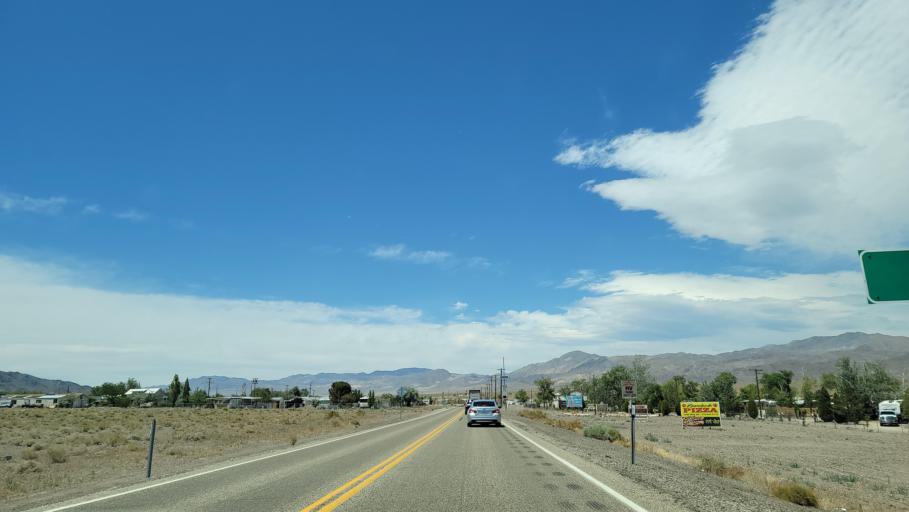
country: US
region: Nevada
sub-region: Mineral County
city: Hawthorne
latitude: 38.3833
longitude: -118.1068
